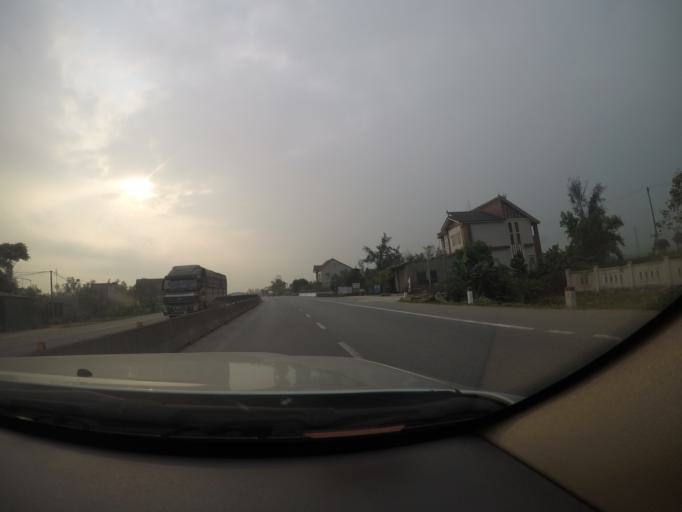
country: VN
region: Ha Tinh
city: Cam Xuyen
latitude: 18.2349
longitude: 106.0237
